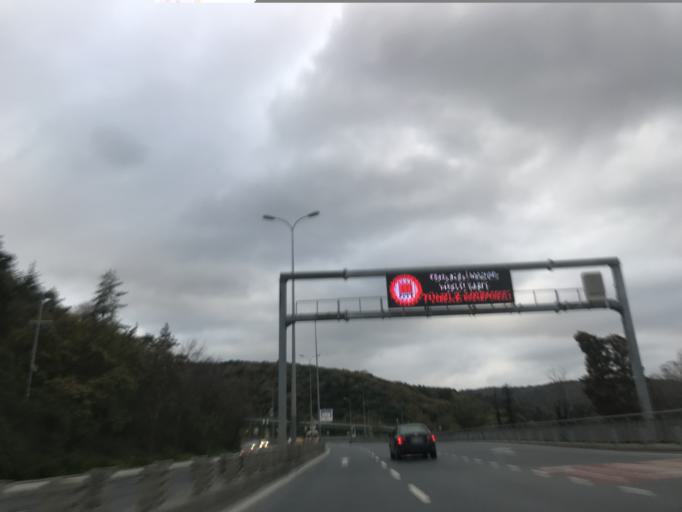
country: TR
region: Istanbul
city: Arikoey
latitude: 41.1529
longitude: 29.0334
